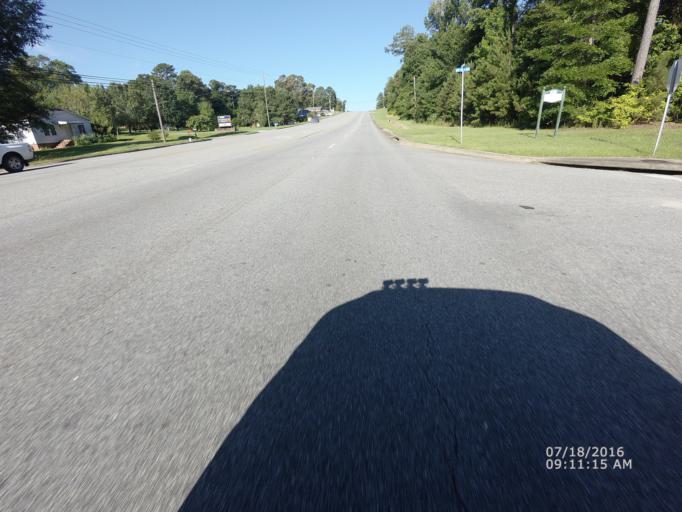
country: US
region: Alabama
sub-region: Chambers County
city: Huguley
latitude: 32.8497
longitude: -85.2092
